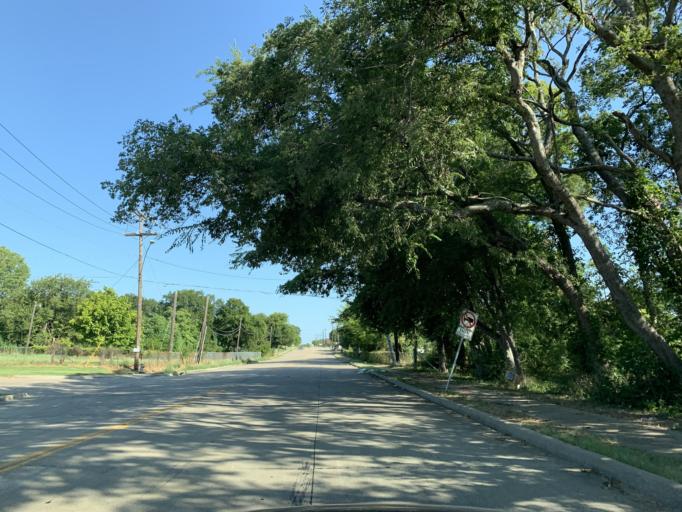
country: US
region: Texas
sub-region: Dallas County
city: Hutchins
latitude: 32.6637
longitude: -96.7417
